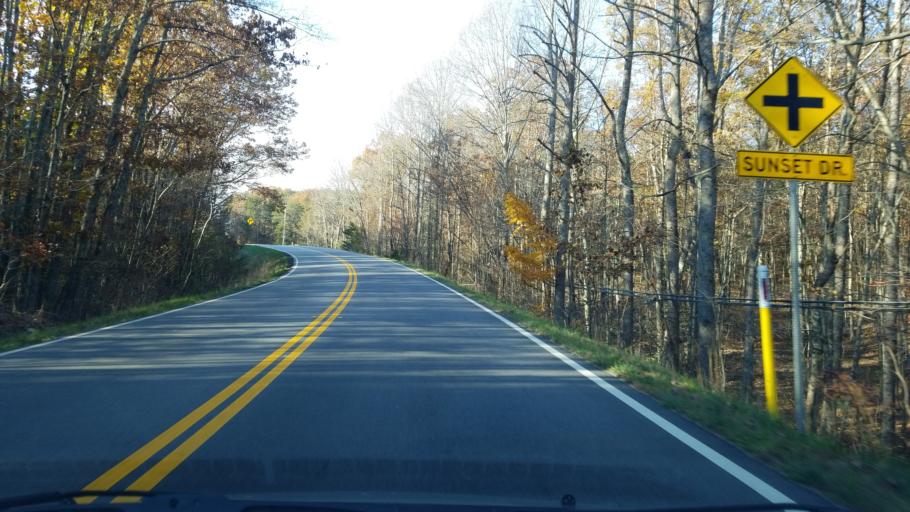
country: US
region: Georgia
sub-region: Dade County
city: Trenton
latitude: 34.8237
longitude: -85.5005
